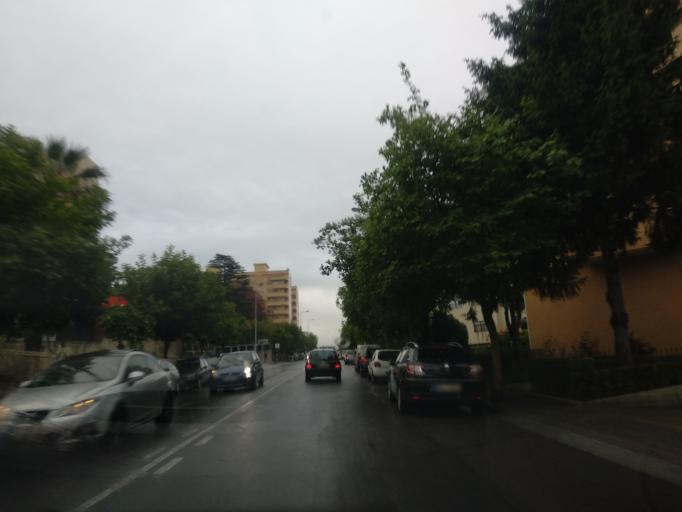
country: PT
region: Porto
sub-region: Gondomar
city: Rio Tinto
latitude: 41.1763
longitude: -8.5582
